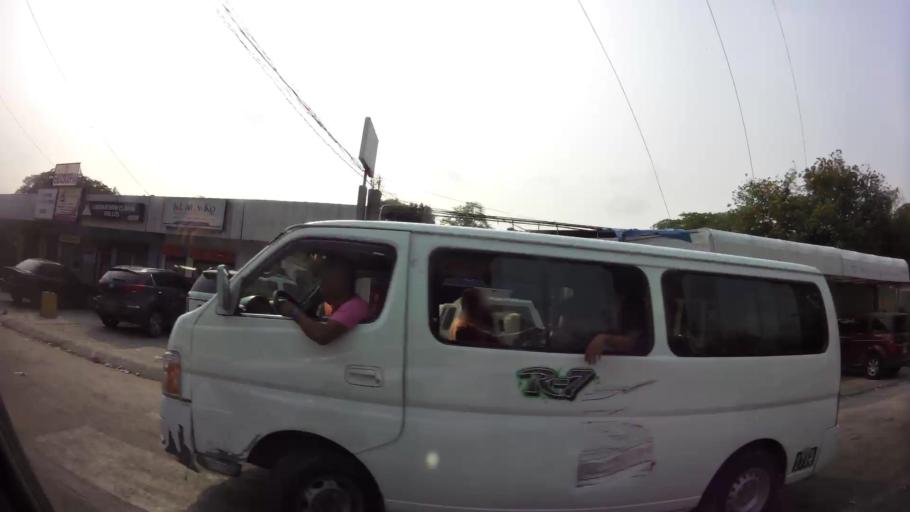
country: HN
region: Cortes
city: El Zapotal del Norte
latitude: 15.5238
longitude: -88.0405
